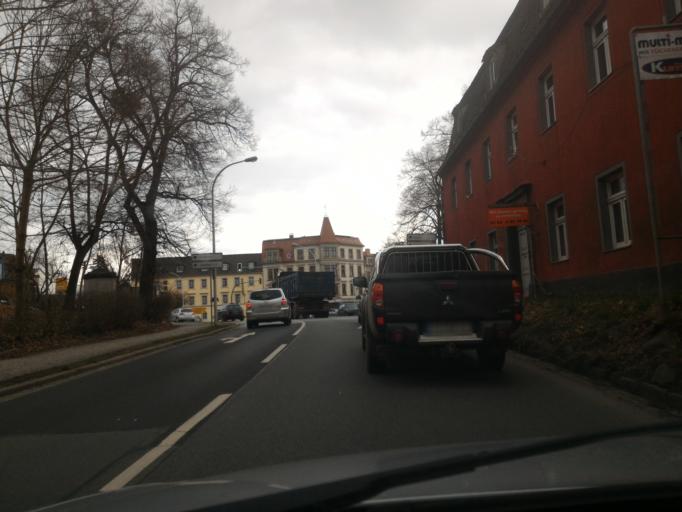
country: DE
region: Saxony
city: Zittau
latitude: 50.8930
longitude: 14.8088
